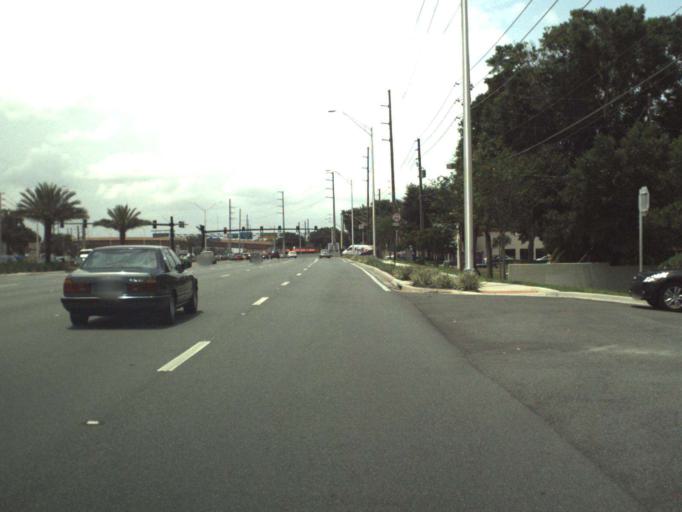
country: US
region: Florida
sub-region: Seminole County
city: Fern Park
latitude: 28.6427
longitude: -81.3221
